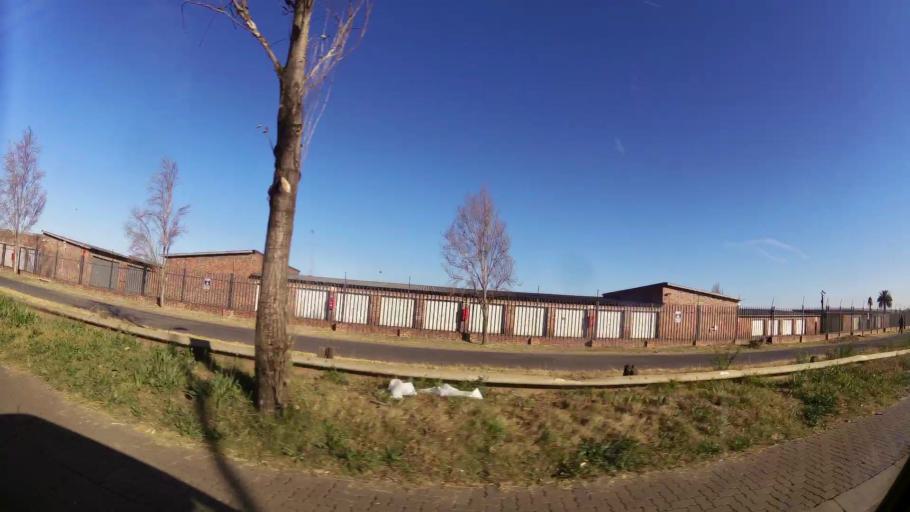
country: ZA
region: Gauteng
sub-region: Ekurhuleni Metropolitan Municipality
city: Germiston
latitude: -26.2907
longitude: 28.1378
